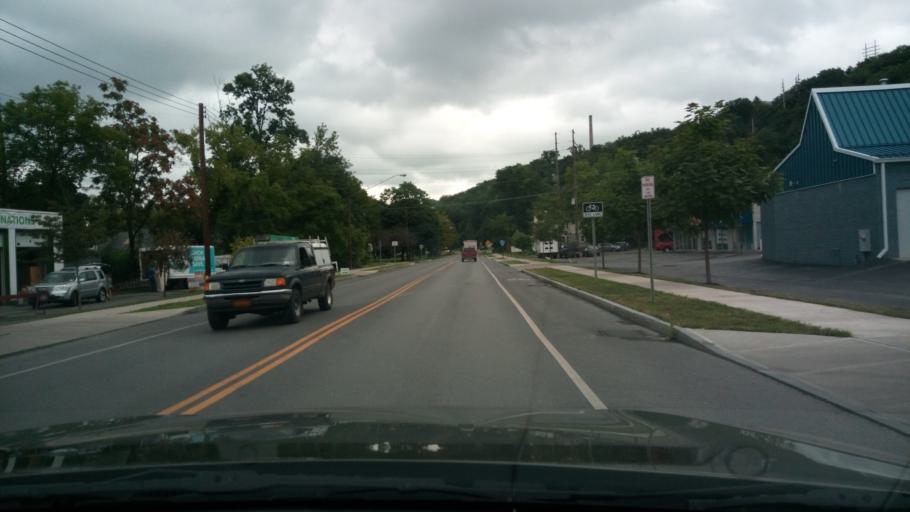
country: US
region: New York
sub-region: Tompkins County
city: South Hill
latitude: 42.4301
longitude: -76.5044
